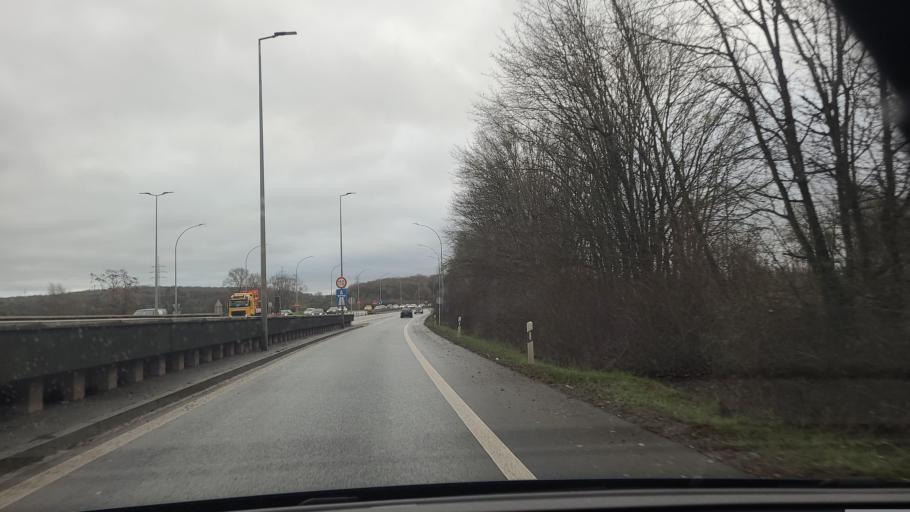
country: LU
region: Luxembourg
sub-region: Canton de Capellen
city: Bascharage
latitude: 49.5591
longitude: 5.8971
